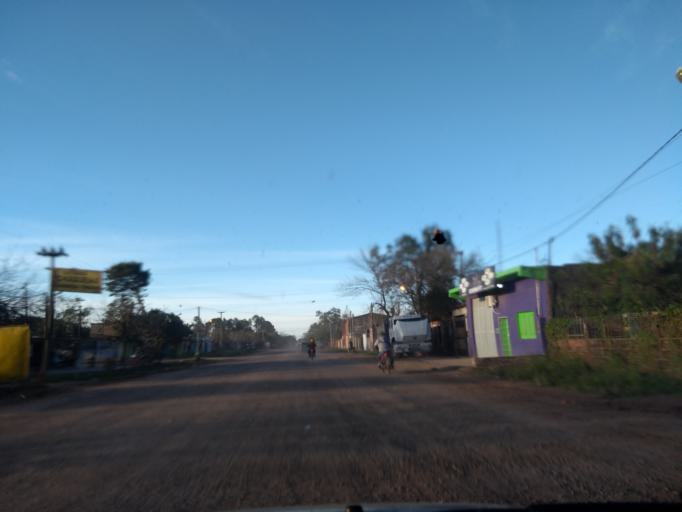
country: AR
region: Chaco
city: Resistencia
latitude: -27.4942
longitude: -58.9774
